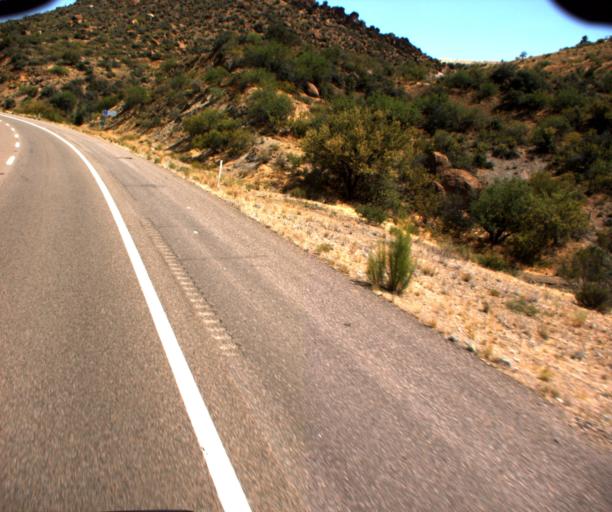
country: US
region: Arizona
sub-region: Gila County
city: Claypool
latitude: 33.4537
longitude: -110.8434
